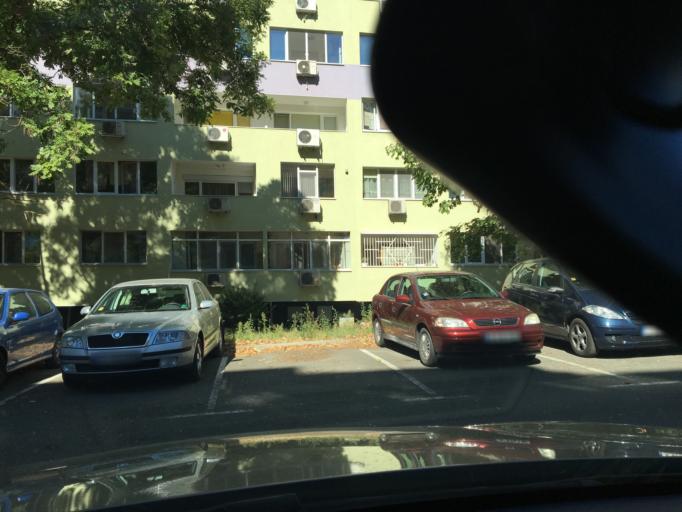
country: BG
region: Burgas
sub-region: Obshtina Burgas
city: Burgas
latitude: 42.5143
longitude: 27.4582
